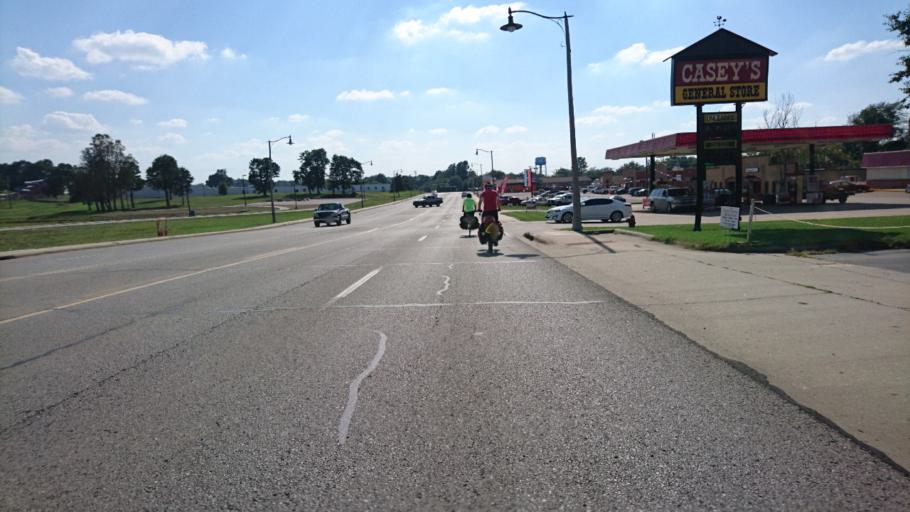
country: US
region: Missouri
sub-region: Laclede County
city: Lebanon
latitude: 37.6710
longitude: -92.6645
